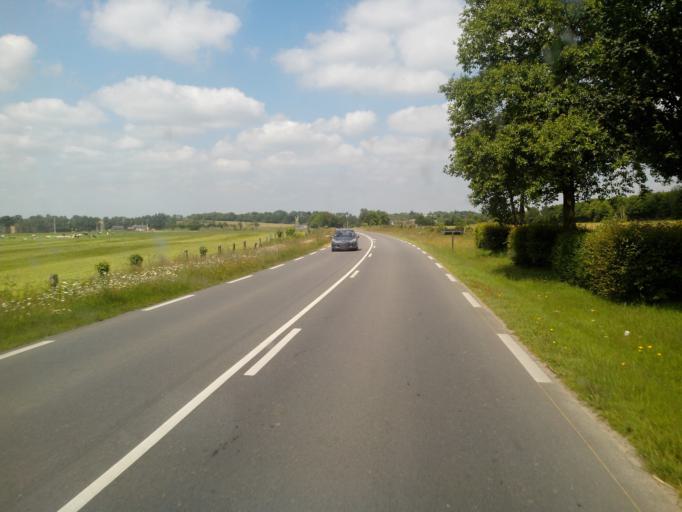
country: FR
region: Brittany
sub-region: Departement d'Ille-et-Vilaine
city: Saint-Germain-en-Cogles
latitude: 48.3924
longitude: -1.2854
